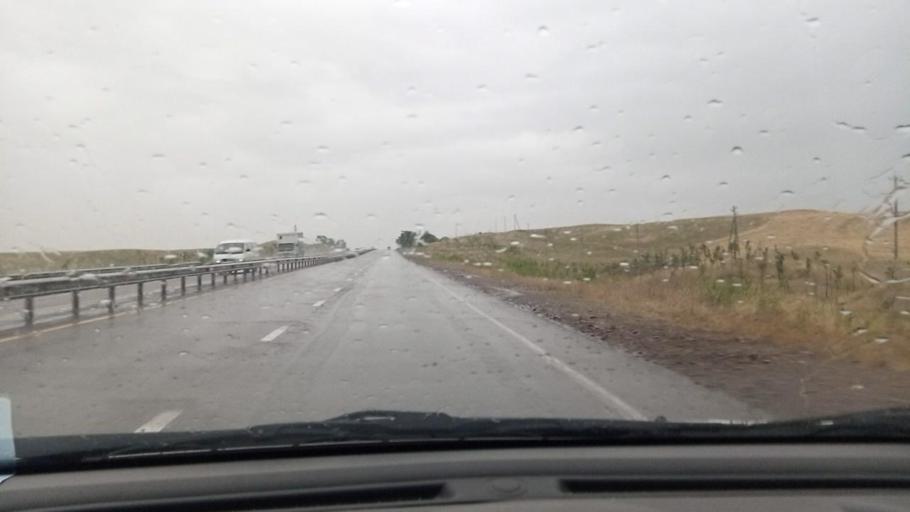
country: UZ
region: Toshkent
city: Ohangaron
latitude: 40.9669
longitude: 69.5508
